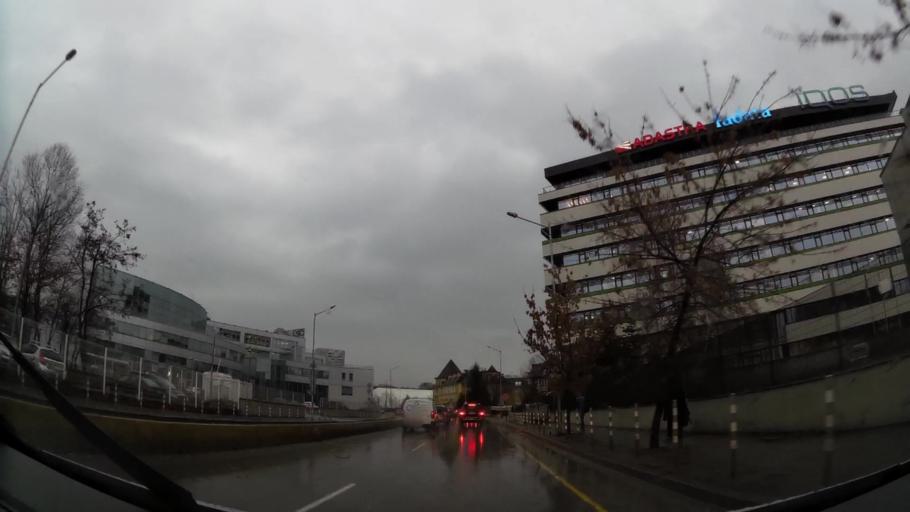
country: BG
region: Sofia-Capital
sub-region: Stolichna Obshtina
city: Sofia
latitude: 42.6650
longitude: 23.3265
